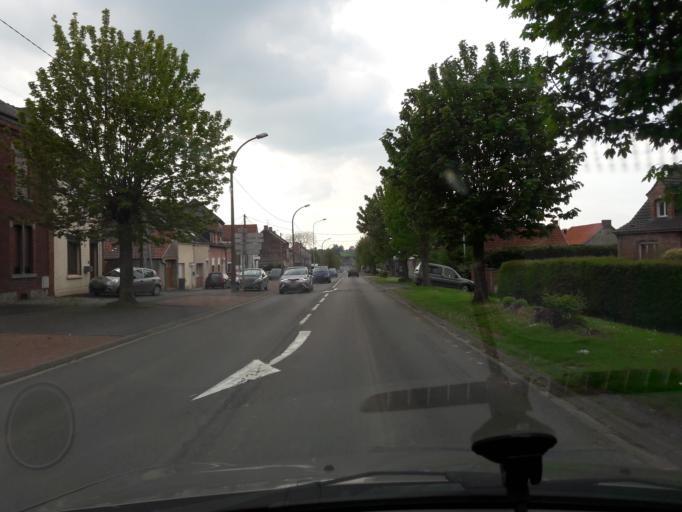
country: FR
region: Nord-Pas-de-Calais
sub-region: Departement du Nord
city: Ferriere-la-Grande
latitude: 50.2600
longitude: 4.0037
